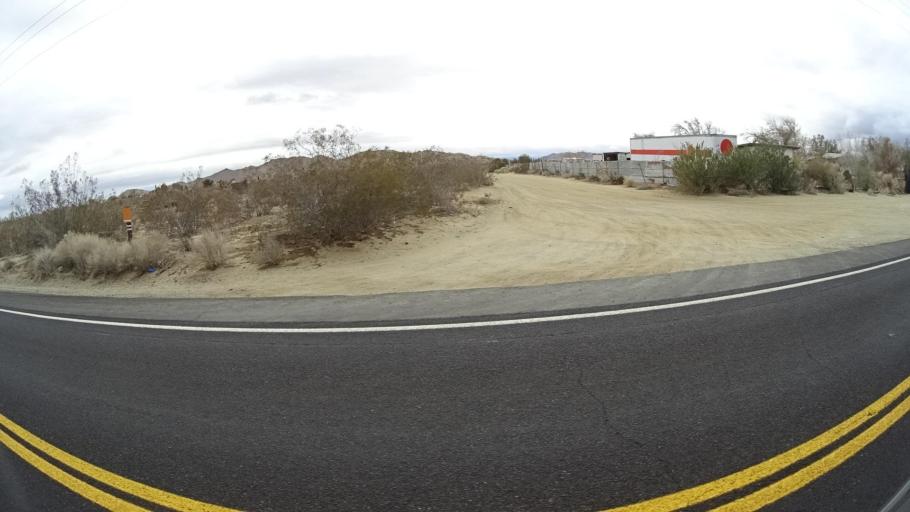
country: US
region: California
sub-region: Kern County
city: Rosamond
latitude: 34.9510
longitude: -118.2517
